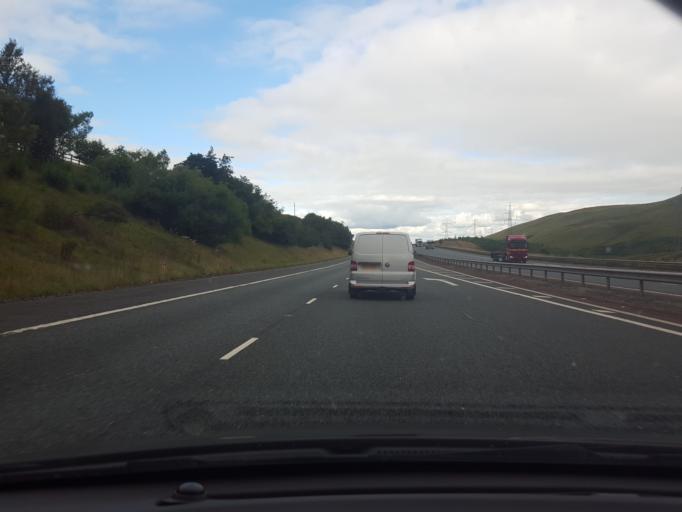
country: GB
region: Scotland
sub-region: South Lanarkshire
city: Douglas
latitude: 55.5521
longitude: -3.8011
